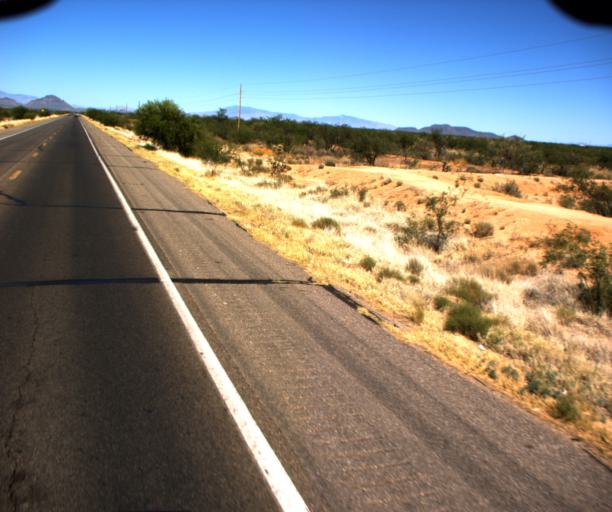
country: US
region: Arizona
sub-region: Pima County
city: Three Points
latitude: 32.1080
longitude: -111.2350
